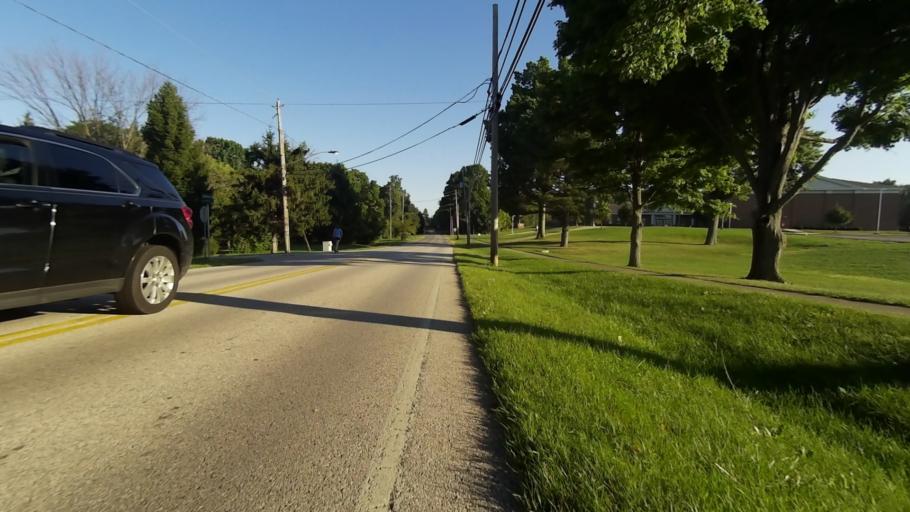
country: US
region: Ohio
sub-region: Portage County
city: Kent
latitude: 41.1672
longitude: -81.3636
